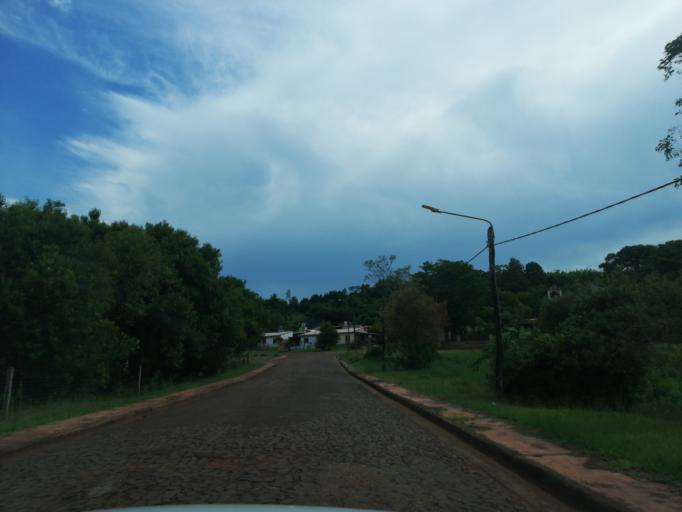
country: AR
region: Misiones
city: Cerro Azul
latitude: -27.5703
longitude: -55.5019
